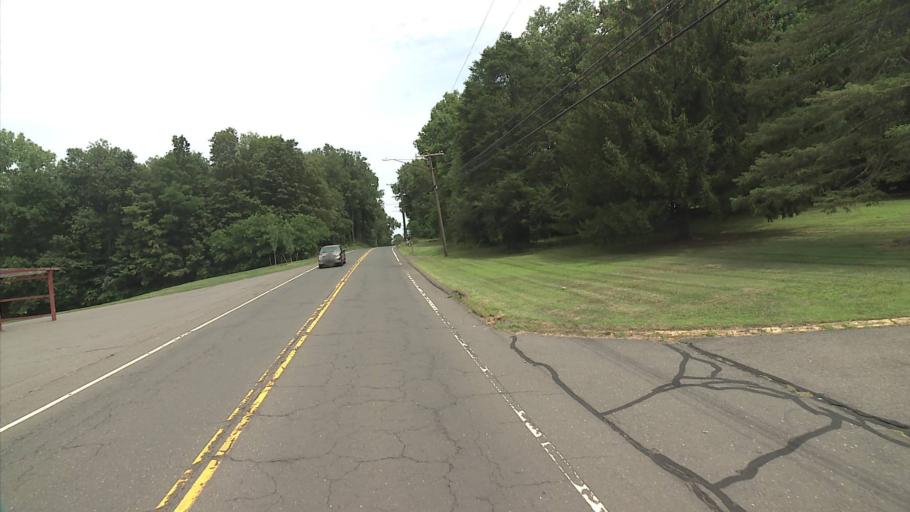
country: US
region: Connecticut
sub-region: Hartford County
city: Kensington
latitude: 41.6071
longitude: -72.7959
